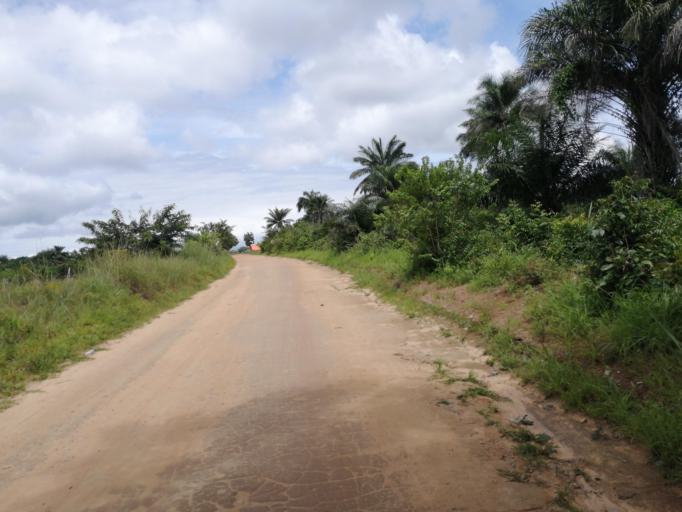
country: SL
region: Northern Province
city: Pepel
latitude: 8.6011
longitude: -13.0541
